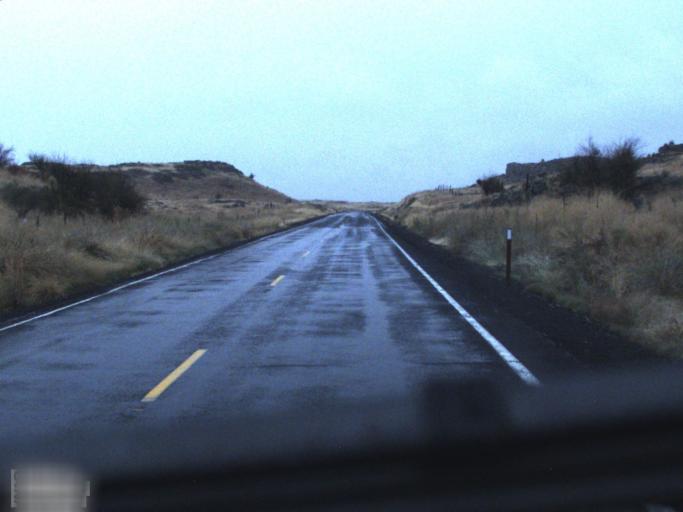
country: US
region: Washington
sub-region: Spokane County
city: Medical Lake
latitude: 47.2492
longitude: -117.9244
